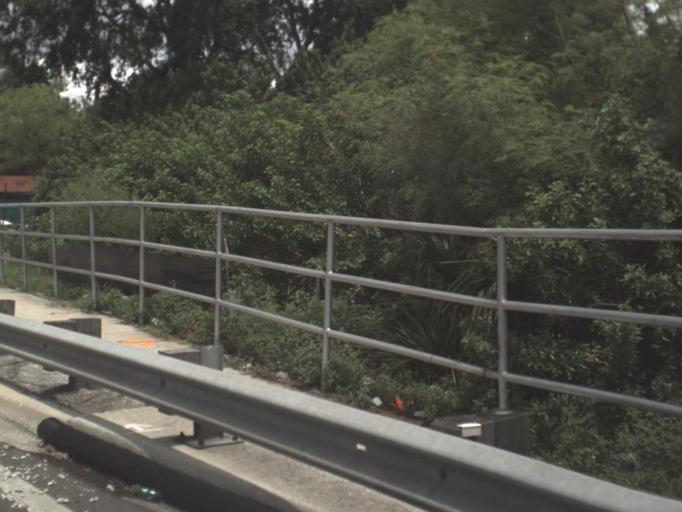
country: US
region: Florida
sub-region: Hillsborough County
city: Town 'n' Country
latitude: 28.0010
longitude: -82.5933
